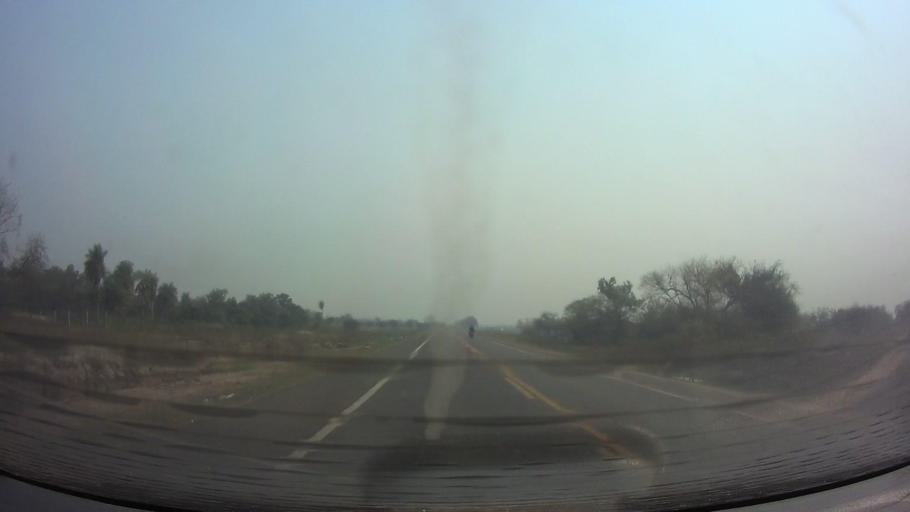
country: PY
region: Central
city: Limpio
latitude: -25.1524
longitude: -57.4790
